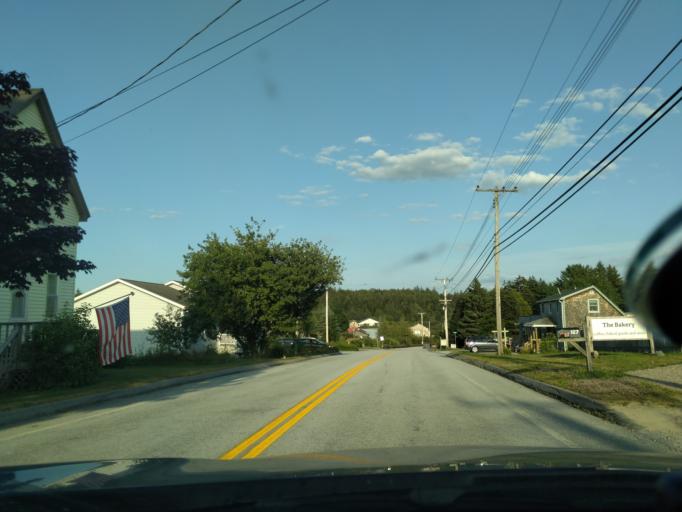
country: US
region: Maine
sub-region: Hancock County
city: Gouldsboro
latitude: 44.3955
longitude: -68.0795
